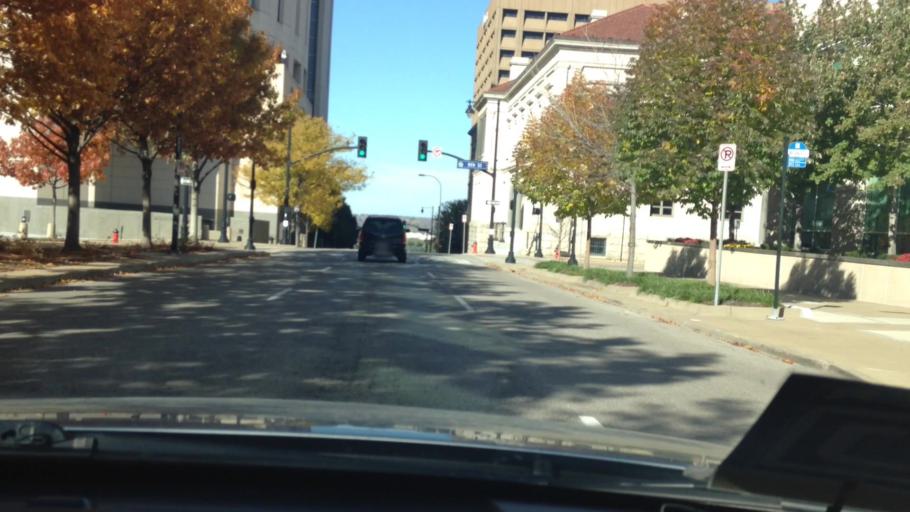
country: US
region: Missouri
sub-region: Jackson County
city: Kansas City
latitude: 39.1029
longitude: -94.5772
